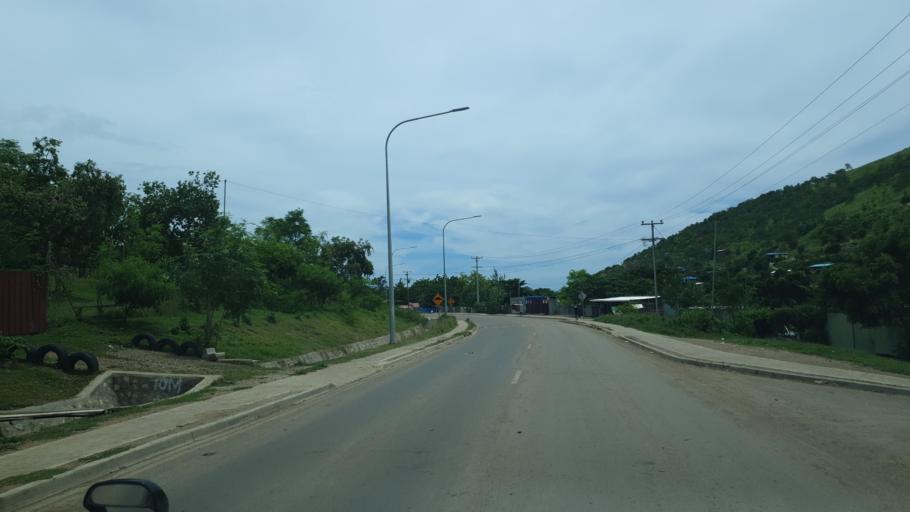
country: PG
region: National Capital
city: Port Moresby
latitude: -9.5276
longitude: 147.2420
